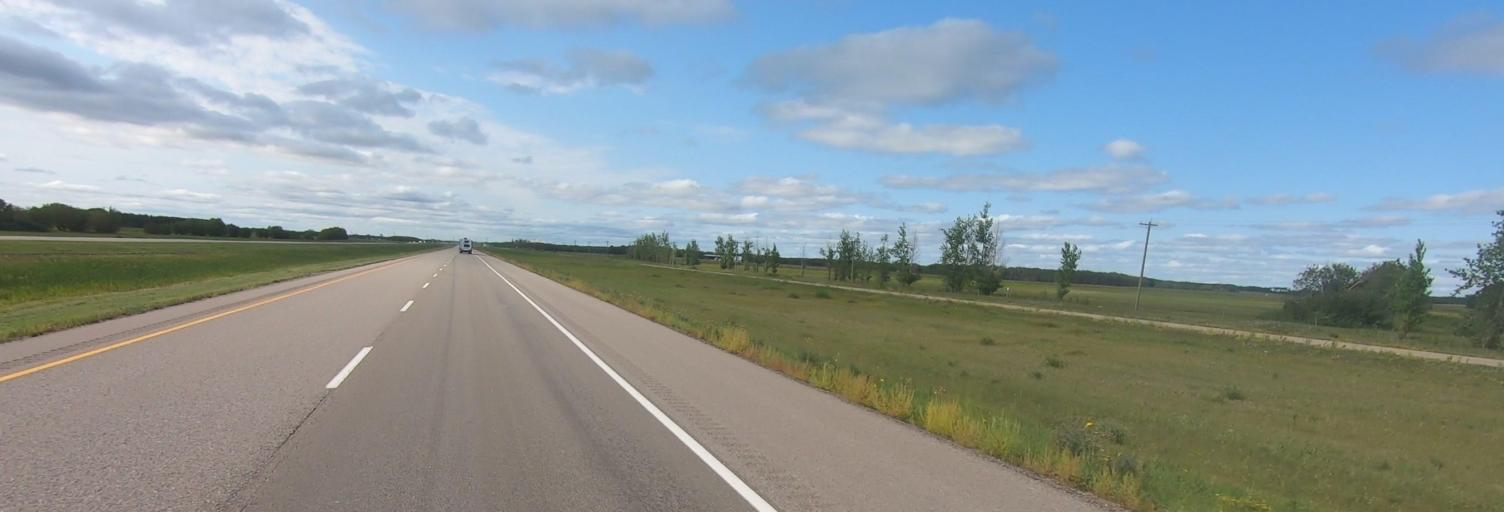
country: CA
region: Manitoba
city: Virden
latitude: 49.8188
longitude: -100.8601
